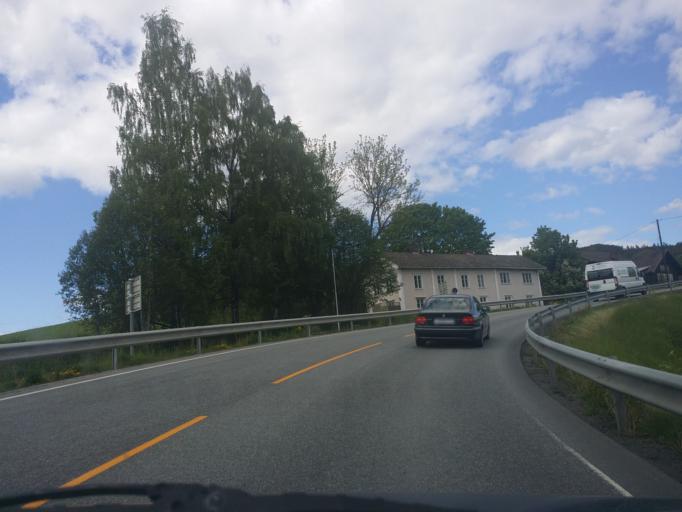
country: NO
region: Oppland
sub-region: Jevnaker
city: Jevnaker
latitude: 60.2547
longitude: 10.4289
